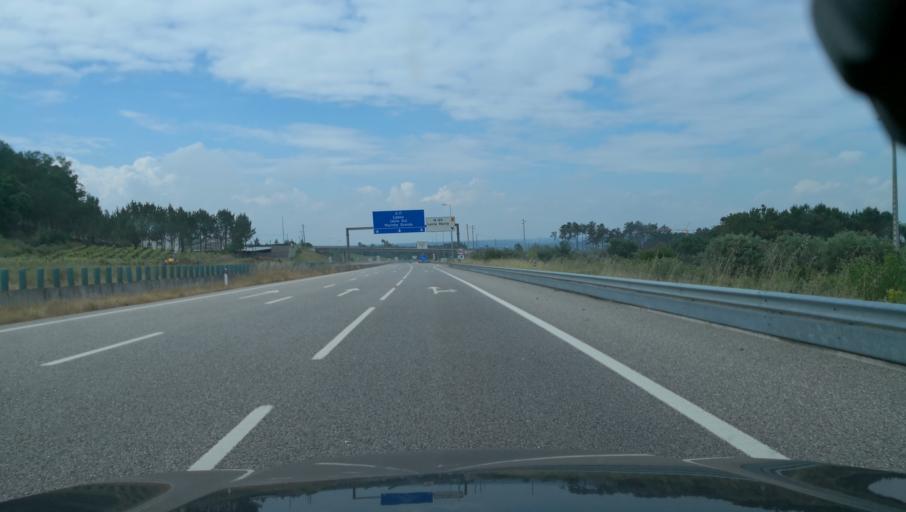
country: PT
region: Leiria
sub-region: Leiria
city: Amor
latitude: 39.8178
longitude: -8.8383
